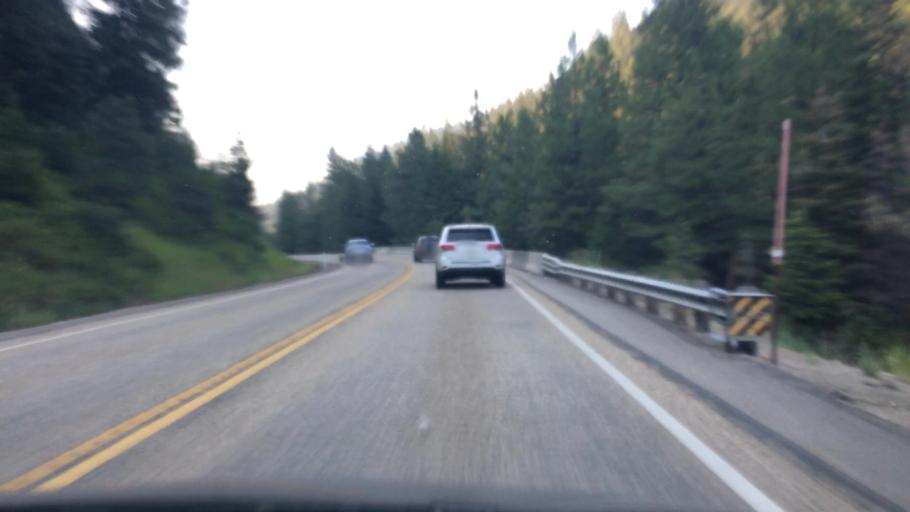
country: US
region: Idaho
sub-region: Valley County
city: Cascade
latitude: 44.2032
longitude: -116.1098
